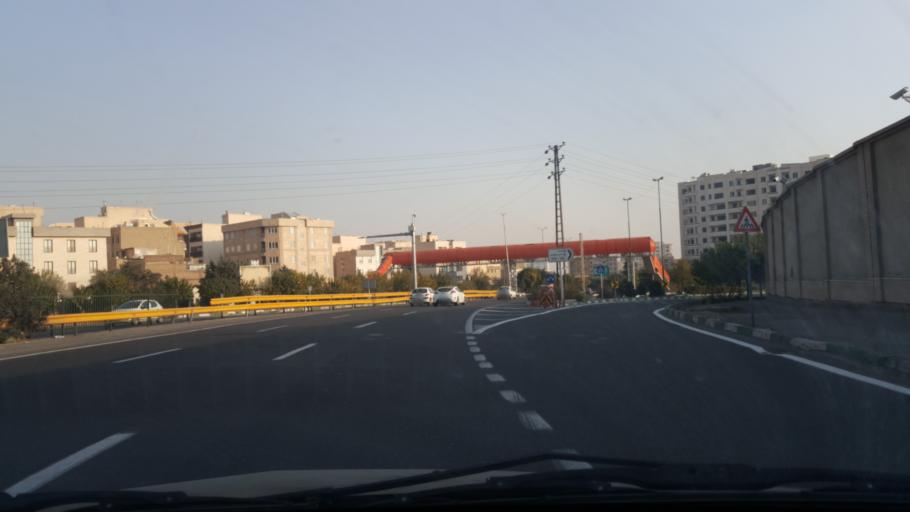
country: IR
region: Tehran
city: Tehran
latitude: 35.7376
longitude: 51.2830
